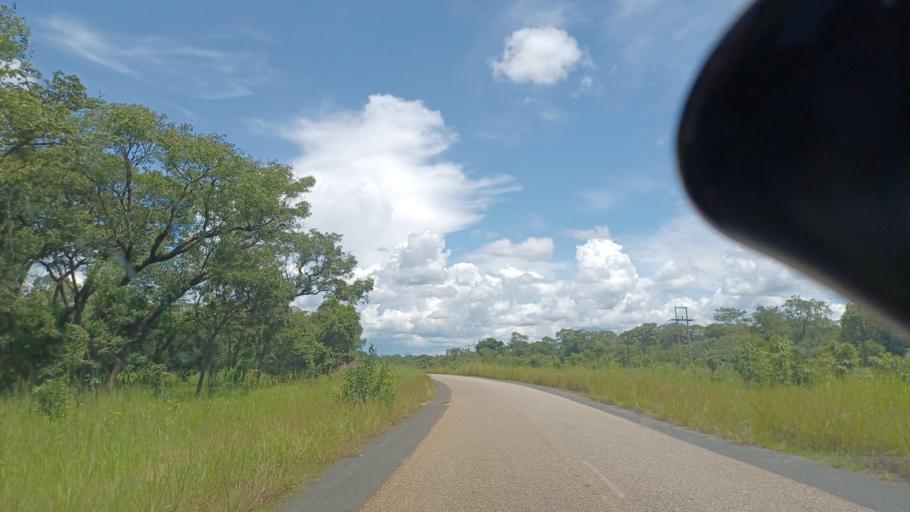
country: ZM
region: North-Western
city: Solwezi
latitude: -12.5790
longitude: 26.1312
